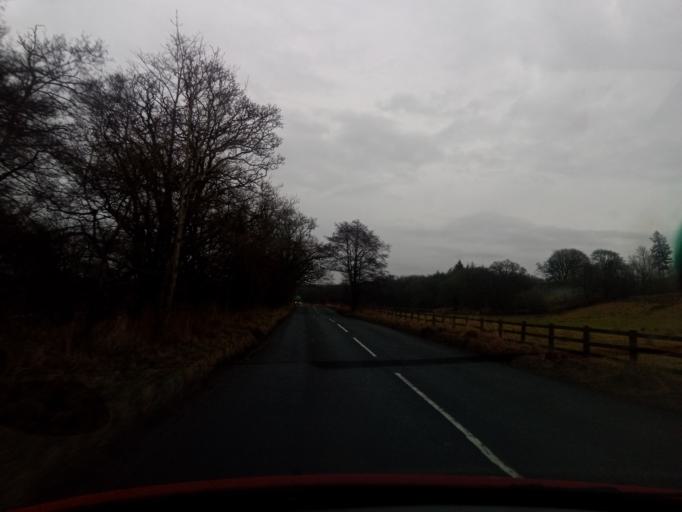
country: GB
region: England
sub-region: Northumberland
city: Rochester
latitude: 55.1661
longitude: -2.4189
